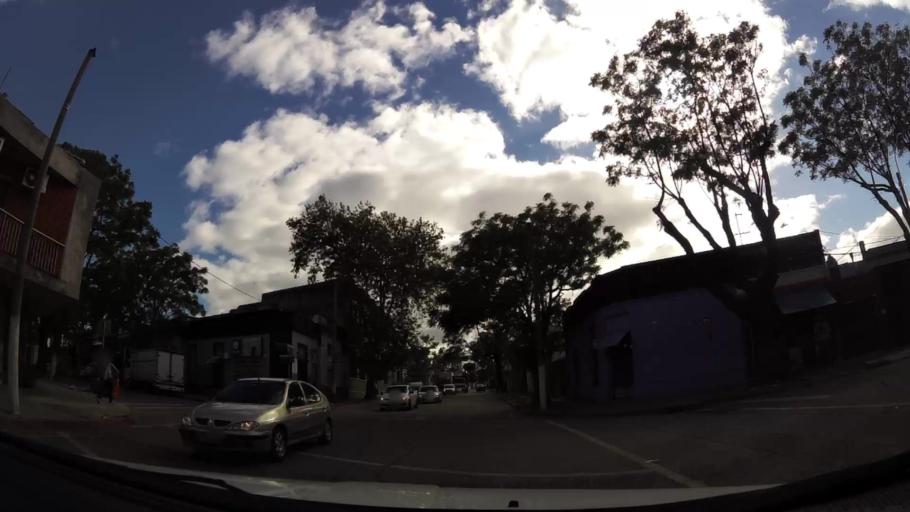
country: UY
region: Montevideo
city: Montevideo
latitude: -34.8860
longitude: -56.1762
